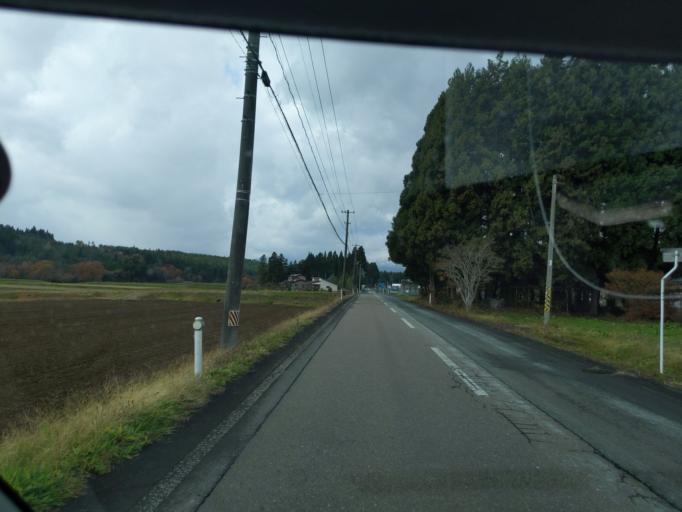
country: JP
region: Iwate
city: Mizusawa
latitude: 39.0852
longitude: 141.0270
